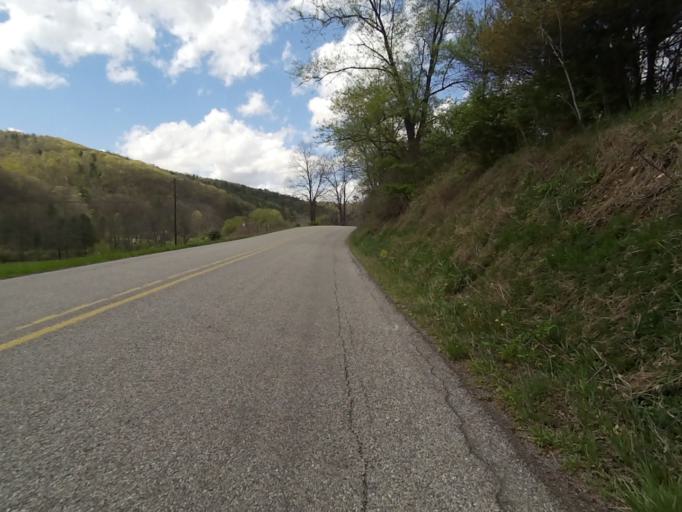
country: US
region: Pennsylvania
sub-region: Centre County
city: Milesburg
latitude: 40.9244
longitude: -77.8683
